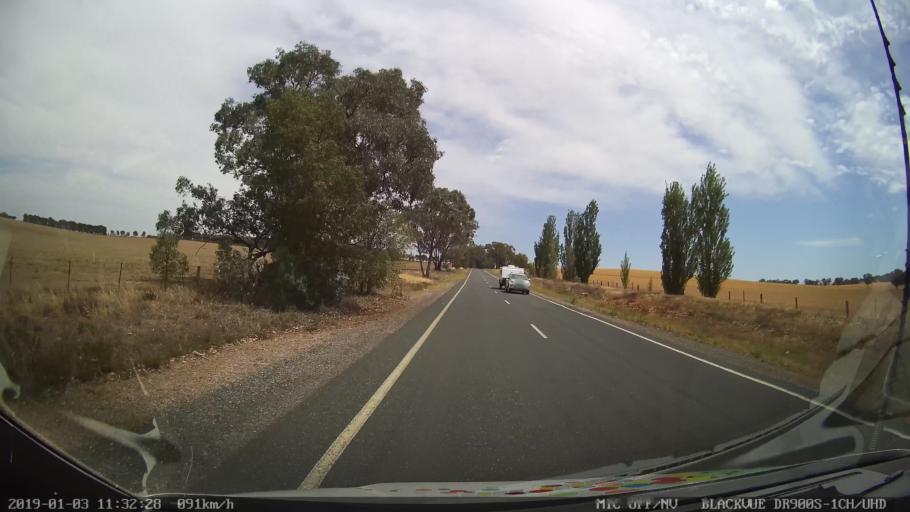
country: AU
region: New South Wales
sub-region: Weddin
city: Grenfell
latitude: -33.9579
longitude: 148.1783
